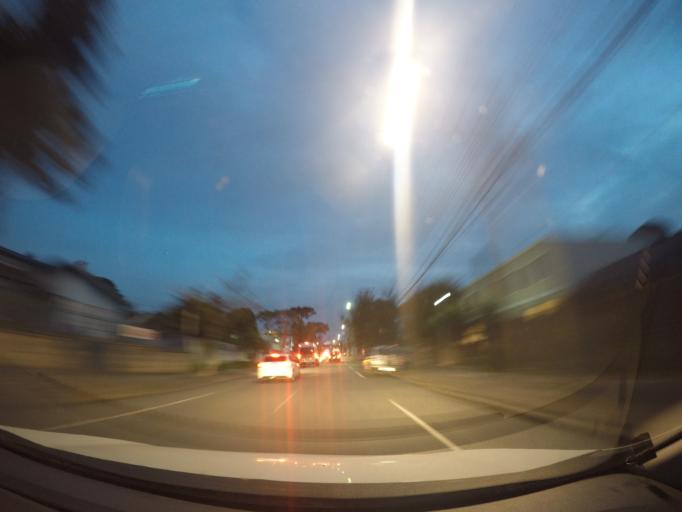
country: BR
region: Parana
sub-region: Curitiba
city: Curitiba
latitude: -25.4205
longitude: -49.2829
